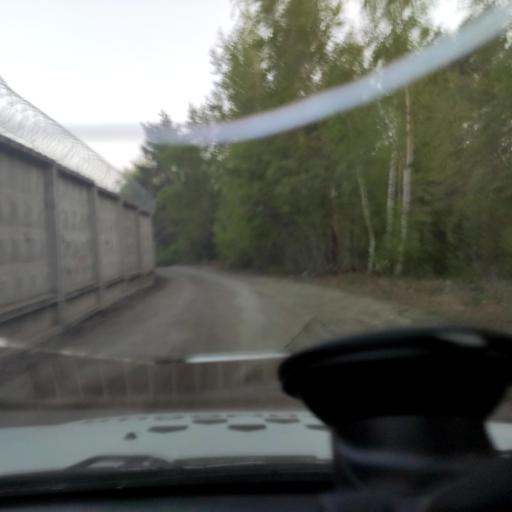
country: RU
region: Perm
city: Perm
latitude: 58.1138
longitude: 56.3429
